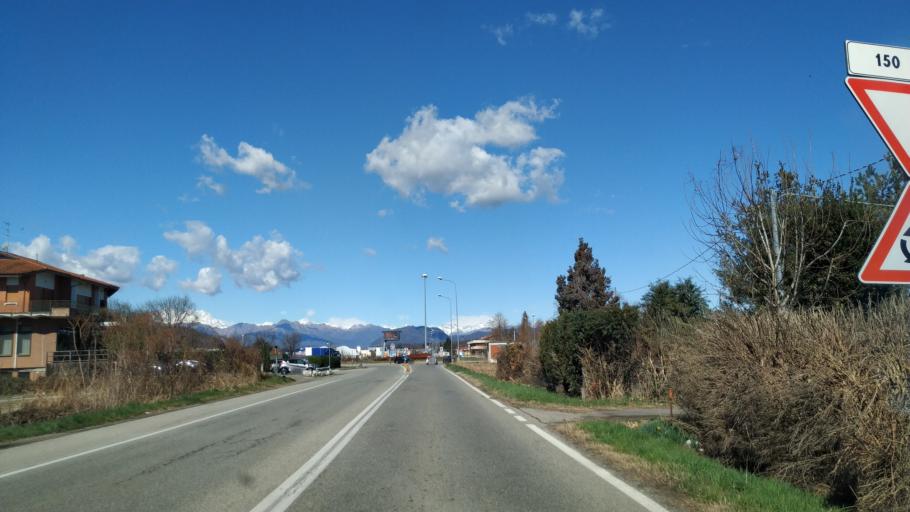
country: IT
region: Piedmont
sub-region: Provincia di Novara
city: Ghemme
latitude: 45.6114
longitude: 8.4093
